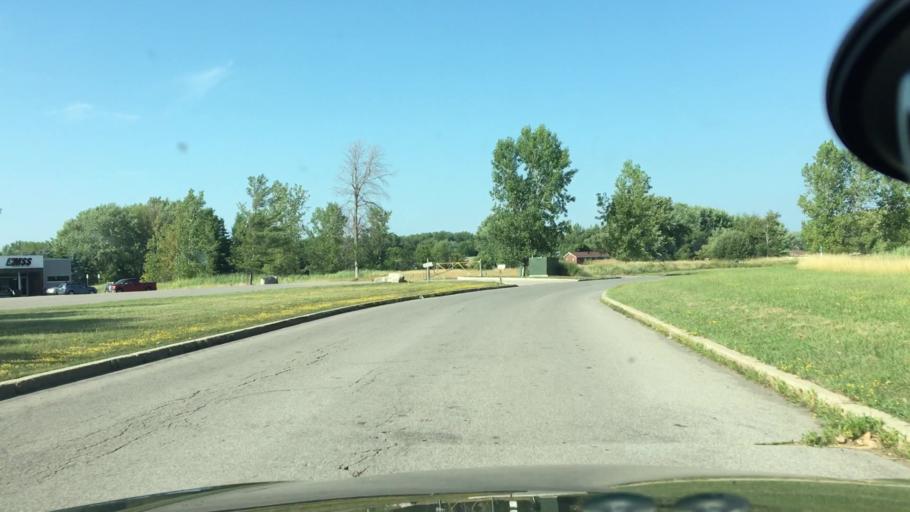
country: US
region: New York
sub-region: Erie County
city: Cheektowaga
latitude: 42.8484
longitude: -78.7417
